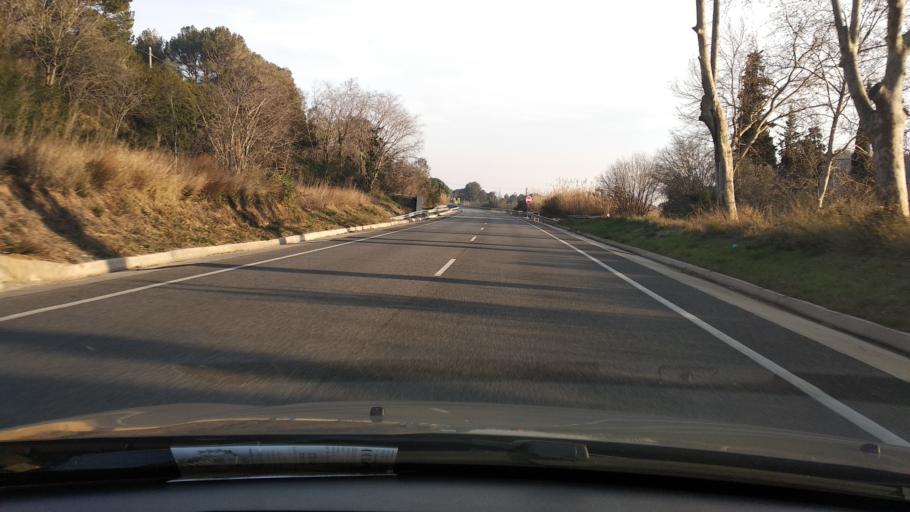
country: ES
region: Catalonia
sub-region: Provincia de Tarragona
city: les Borges del Camp
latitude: 41.1864
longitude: 1.0042
